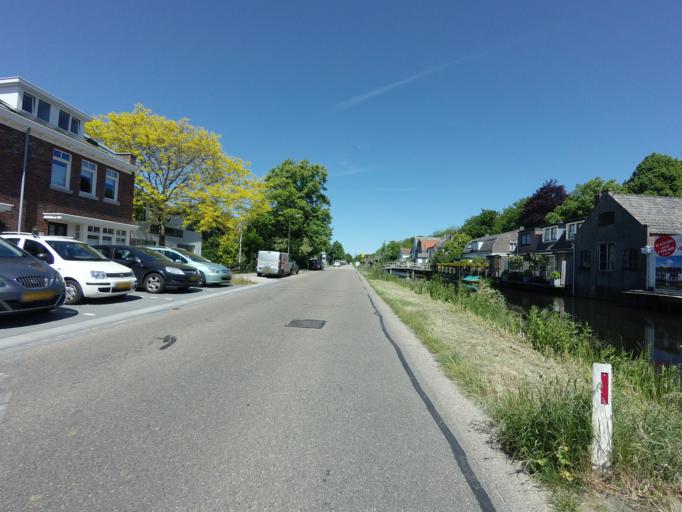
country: NL
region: North Holland
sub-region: Gemeente Wijdemeren
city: Kortenhoef
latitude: 52.2432
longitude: 5.1209
